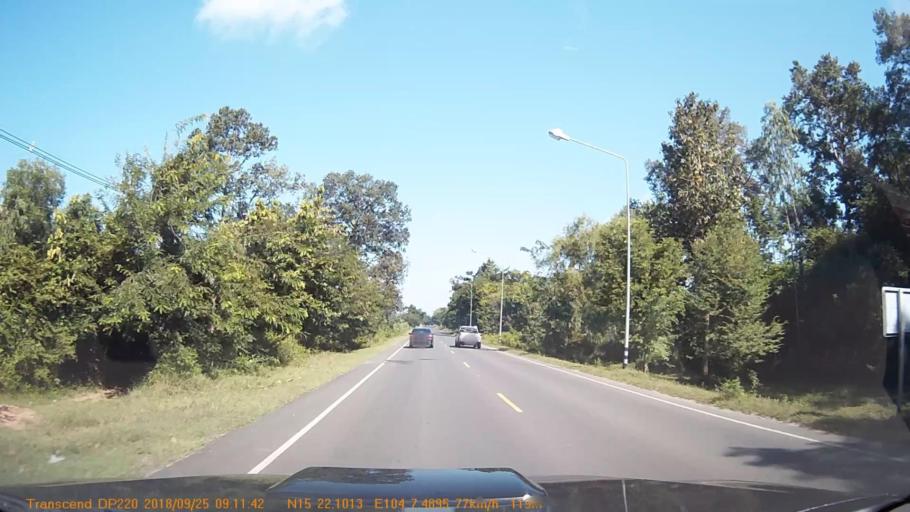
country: TH
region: Sisaket
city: Rasi Salai
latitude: 15.3683
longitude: 104.1248
